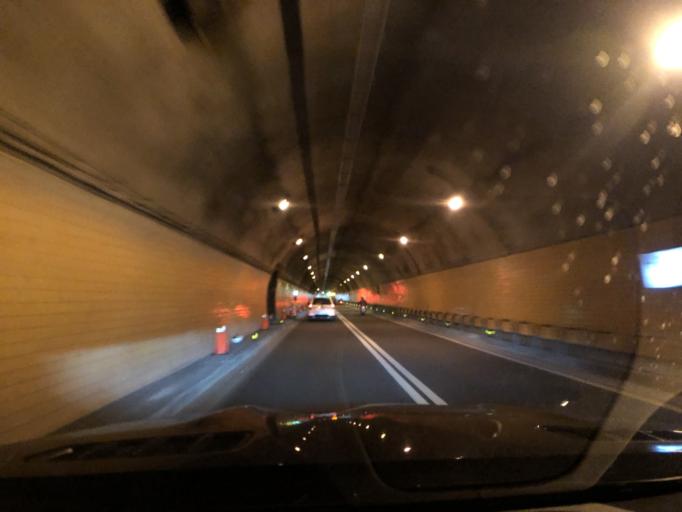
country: TW
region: Taipei
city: Taipei
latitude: 24.9945
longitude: 121.5516
